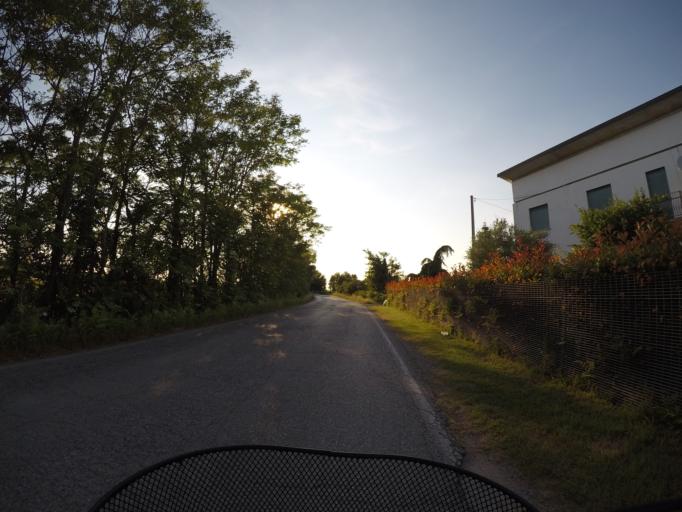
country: IT
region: Veneto
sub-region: Provincia di Rovigo
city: Fratta Polesine
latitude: 45.0287
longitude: 11.6276
